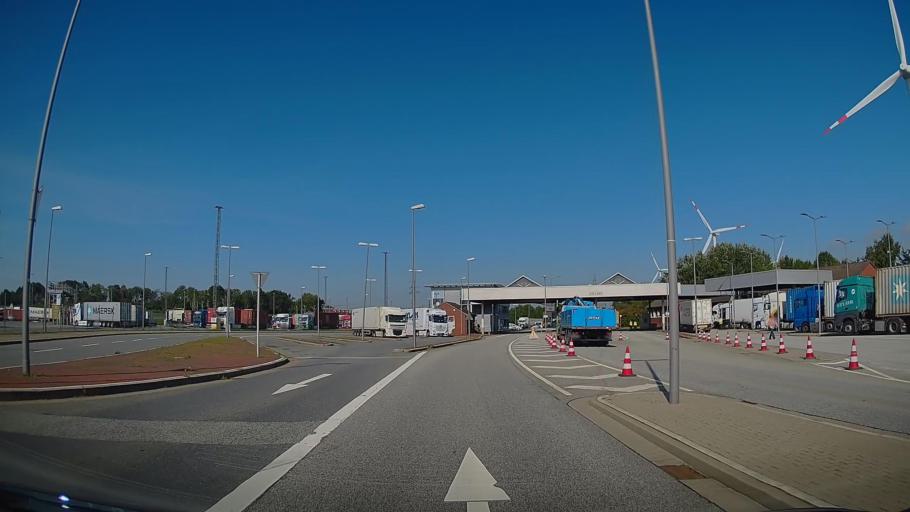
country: DE
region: Lower Saxony
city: Langen
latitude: 53.5945
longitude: 8.5391
